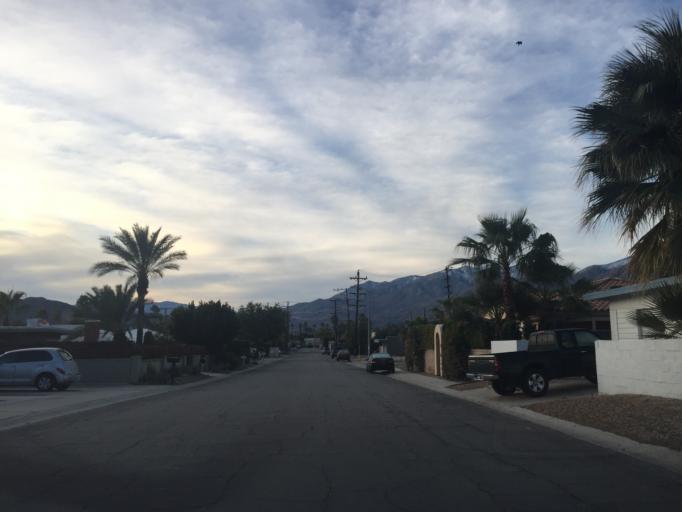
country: US
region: California
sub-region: Riverside County
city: Palm Springs
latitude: 33.8139
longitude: -116.5412
